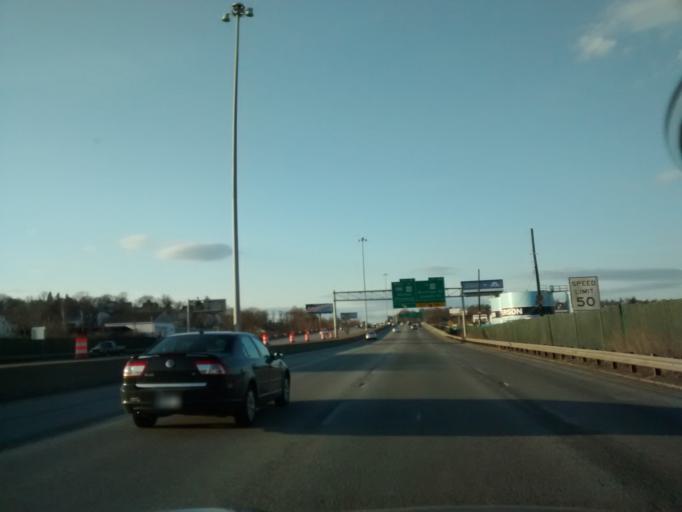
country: US
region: Massachusetts
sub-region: Worcester County
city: Worcester
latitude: 42.2794
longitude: -71.7976
